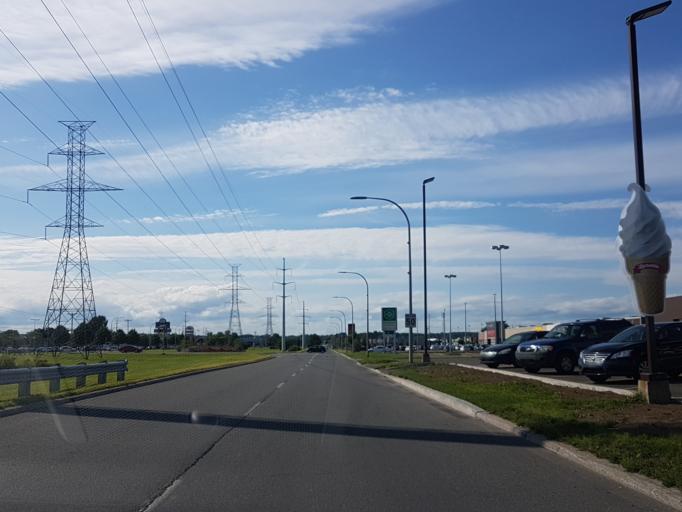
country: CA
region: Quebec
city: Sainte-Catherine
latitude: 46.3259
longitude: -72.5630
